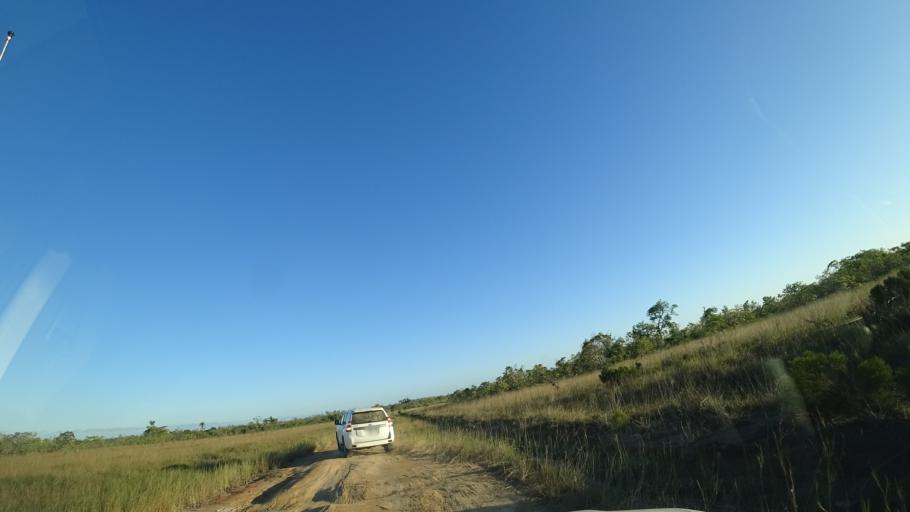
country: MZ
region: Sofala
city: Dondo
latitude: -19.5817
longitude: 35.0869
